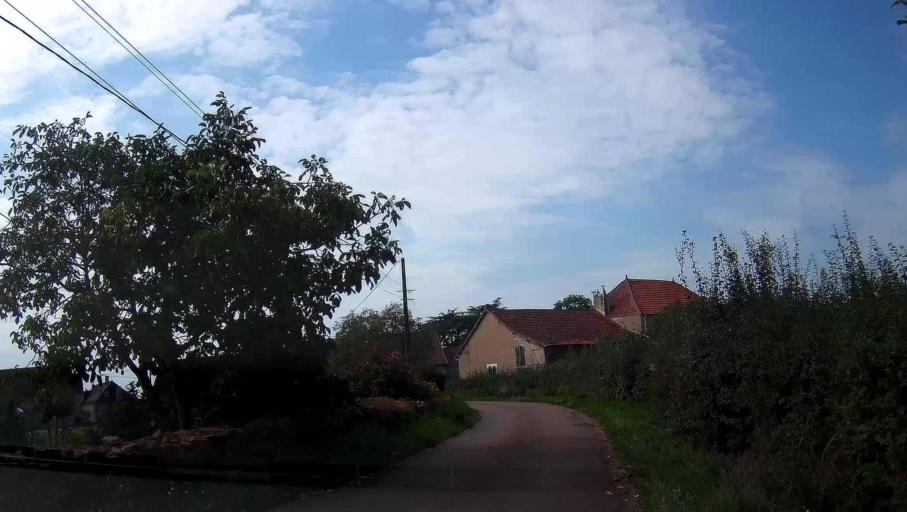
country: FR
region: Bourgogne
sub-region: Departement de Saone-et-Loire
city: Saint-Leger-sur-Dheune
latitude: 46.8931
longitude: 4.6154
